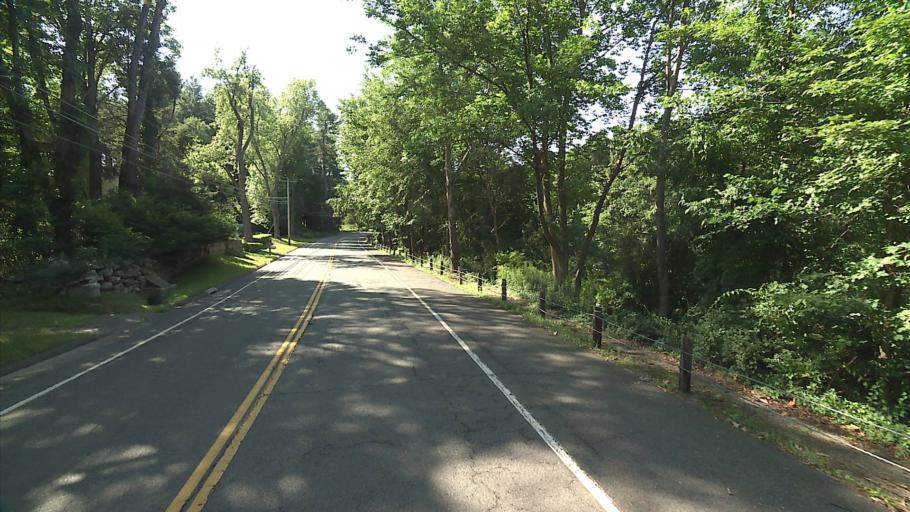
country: US
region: Connecticut
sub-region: Litchfield County
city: Winsted
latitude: 41.9706
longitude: -73.0174
